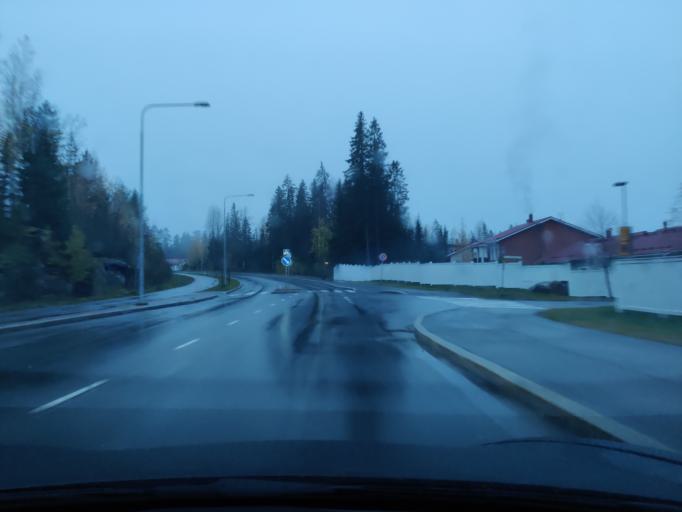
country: FI
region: Northern Savo
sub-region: Kuopio
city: Kuopio
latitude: 62.8302
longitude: 27.7042
